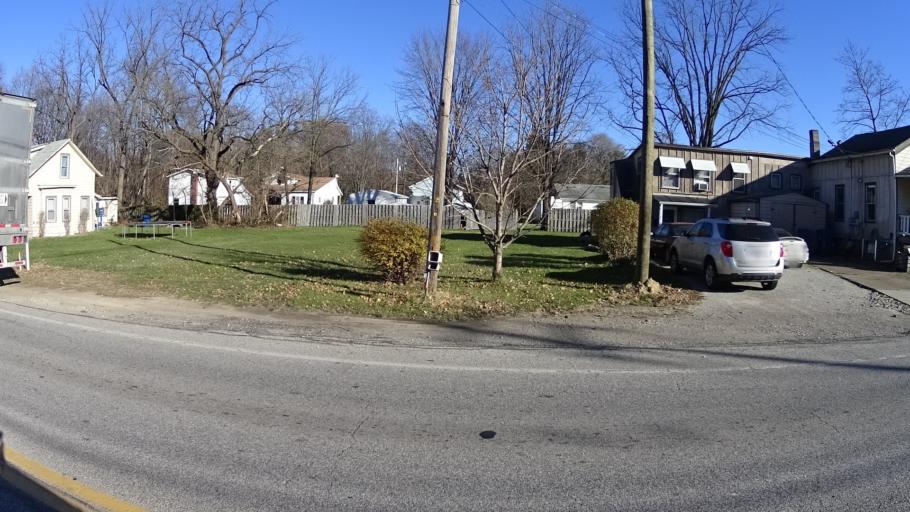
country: US
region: Ohio
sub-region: Lorain County
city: North Ridgeville
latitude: 41.3914
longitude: -82.0187
